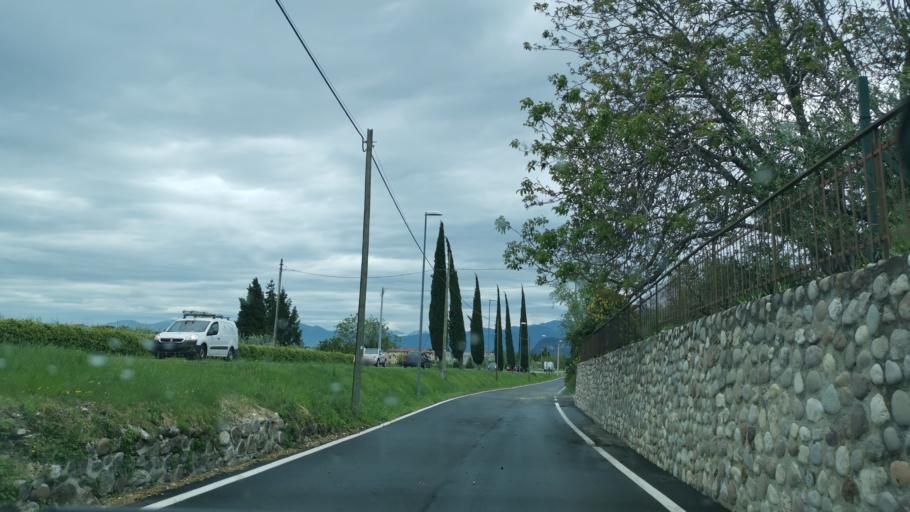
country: IT
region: Veneto
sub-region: Provincia di Verona
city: Bardolino
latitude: 45.5416
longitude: 10.7430
